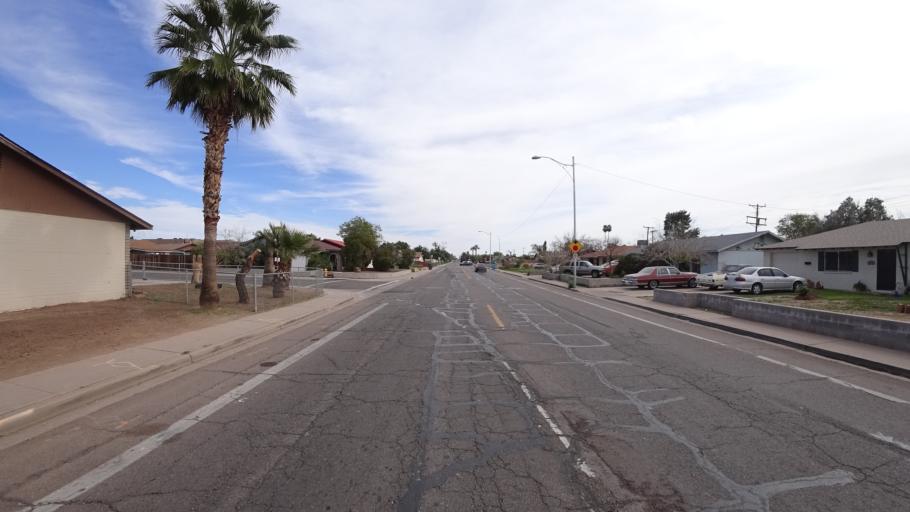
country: US
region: Arizona
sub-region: Maricopa County
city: Glendale
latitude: 33.4877
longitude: -112.1443
